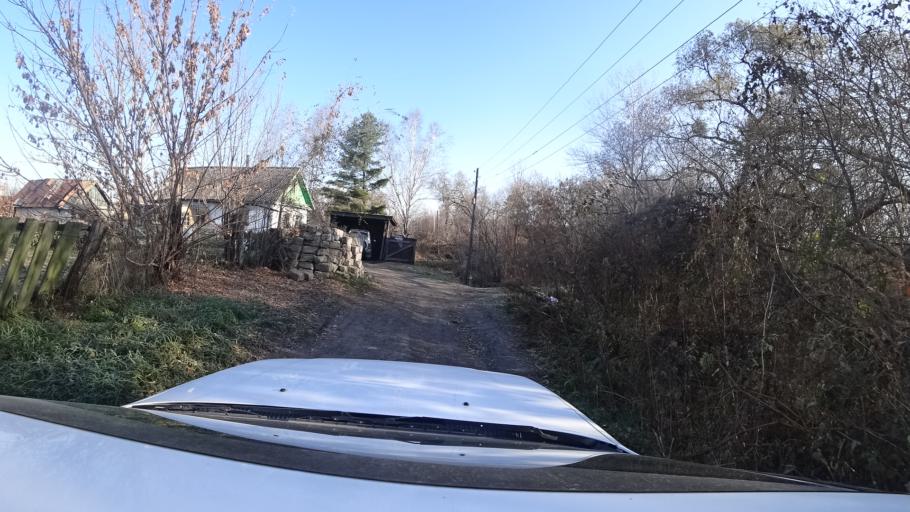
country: RU
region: Primorskiy
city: Lazo
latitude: 45.8774
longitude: 133.6485
